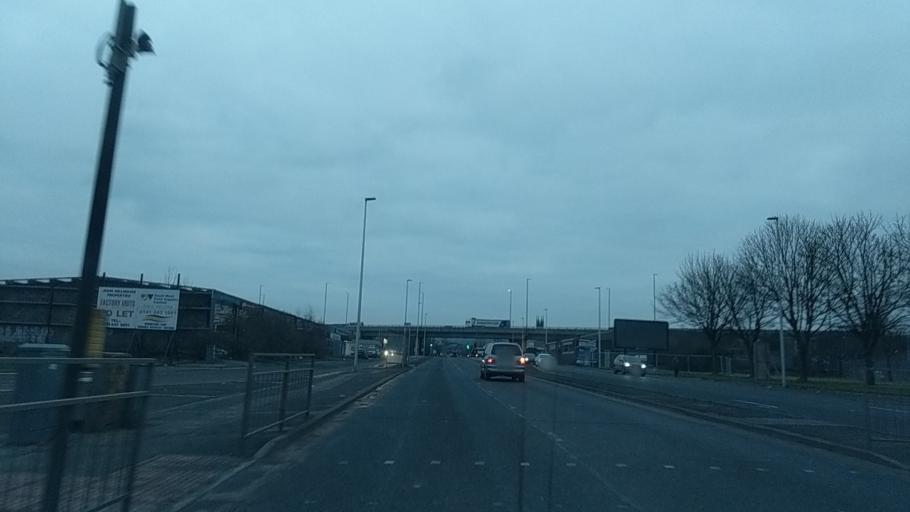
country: GB
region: Scotland
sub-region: South Lanarkshire
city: Rutherglen
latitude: 55.8333
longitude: -4.2238
